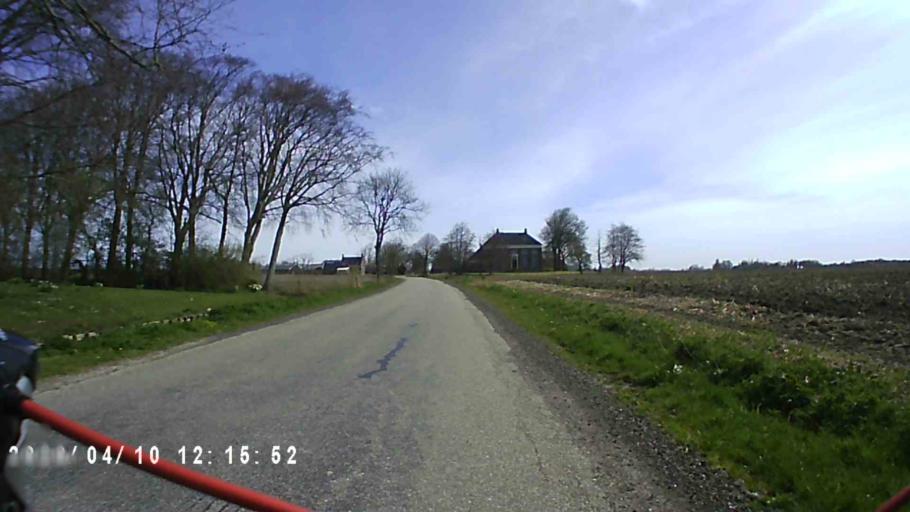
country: NL
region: Groningen
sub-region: Gemeente De Marne
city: Ulrum
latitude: 53.3953
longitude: 6.3782
